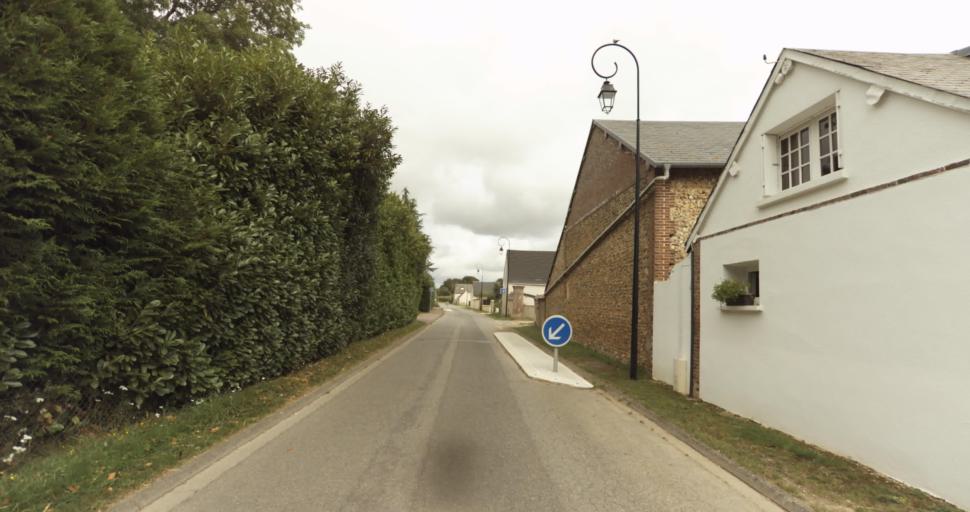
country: FR
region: Haute-Normandie
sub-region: Departement de l'Eure
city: Menilles
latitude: 48.9572
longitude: 1.2971
